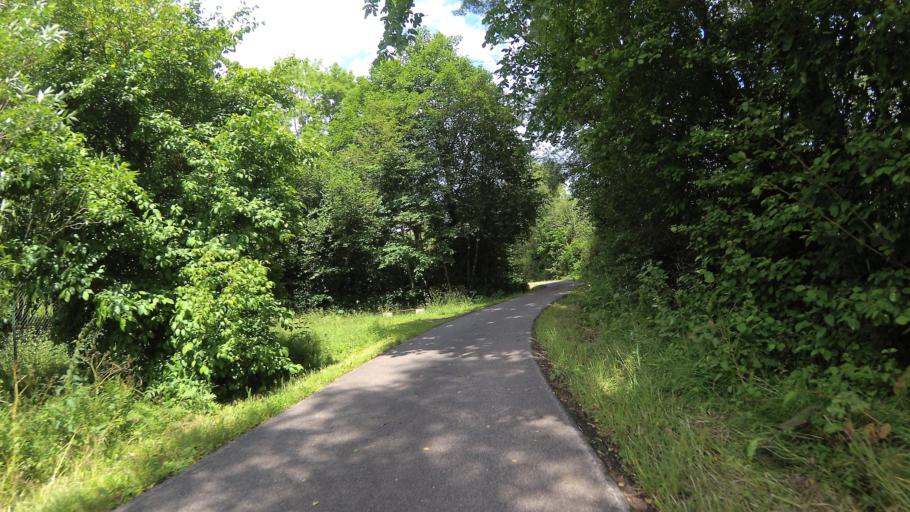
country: DE
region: Saarland
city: Nonnweiler
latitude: 49.5960
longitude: 6.9705
